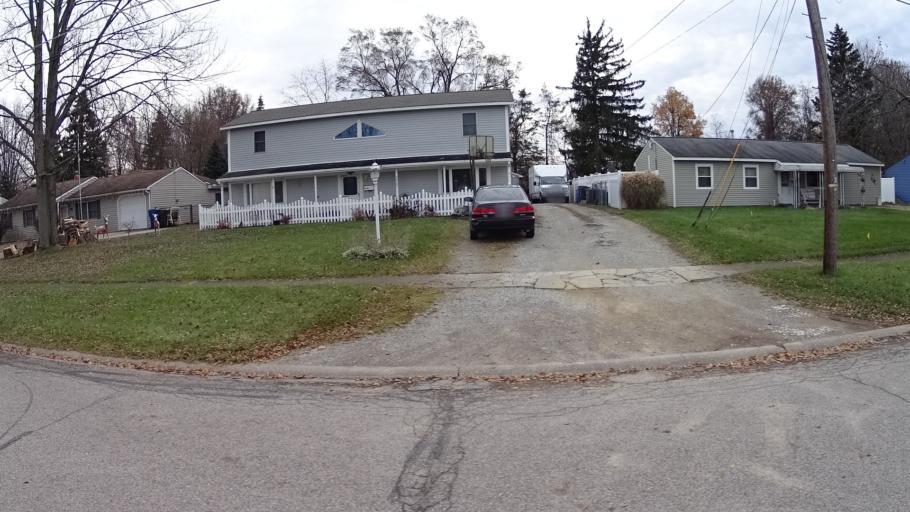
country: US
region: Ohio
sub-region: Lorain County
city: North Ridgeville
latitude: 41.3831
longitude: -82.0029
